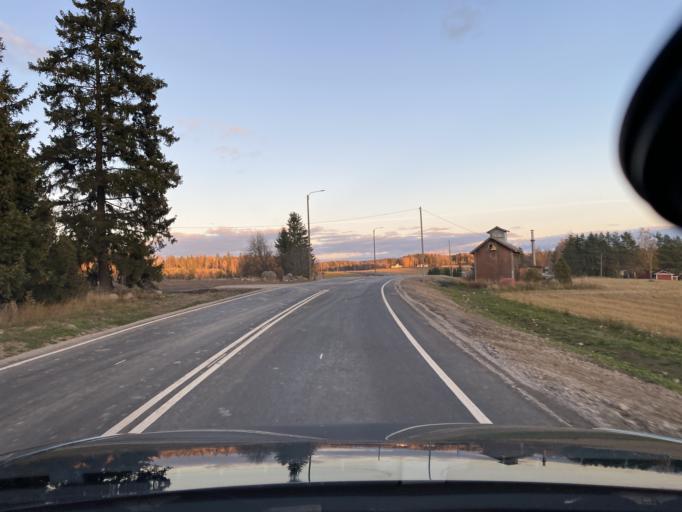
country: FI
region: Pirkanmaa
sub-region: Tampere
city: Vesilahti
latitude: 61.2898
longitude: 23.6050
